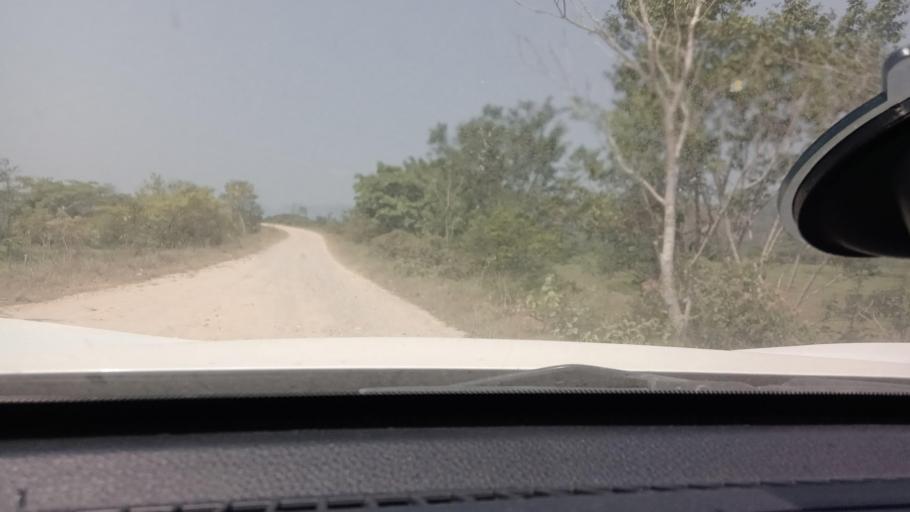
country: MX
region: Tabasco
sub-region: Huimanguillo
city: Francisco Rueda
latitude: 17.5139
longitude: -93.8957
